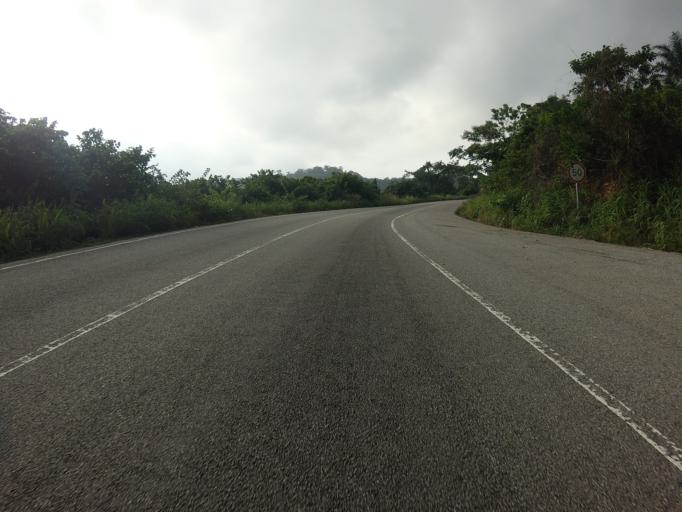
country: GH
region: Volta
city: Ho
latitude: 6.8144
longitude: 0.4204
